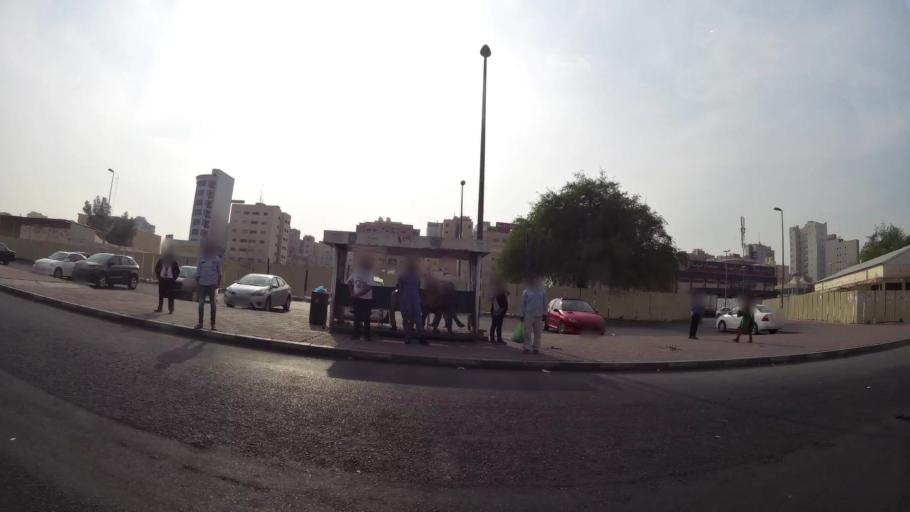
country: KW
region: Al Farwaniyah
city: Al Farwaniyah
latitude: 29.2791
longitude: 47.9613
